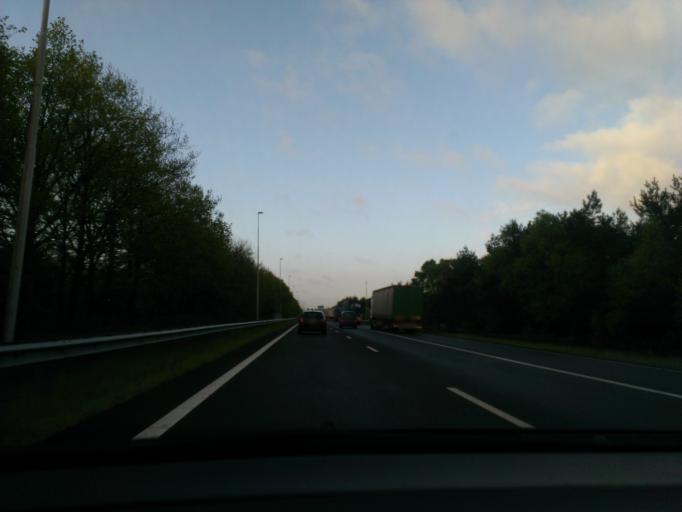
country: NL
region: Gelderland
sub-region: Gemeente Rozendaal
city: Rozendaal
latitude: 52.0499
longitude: 5.9364
